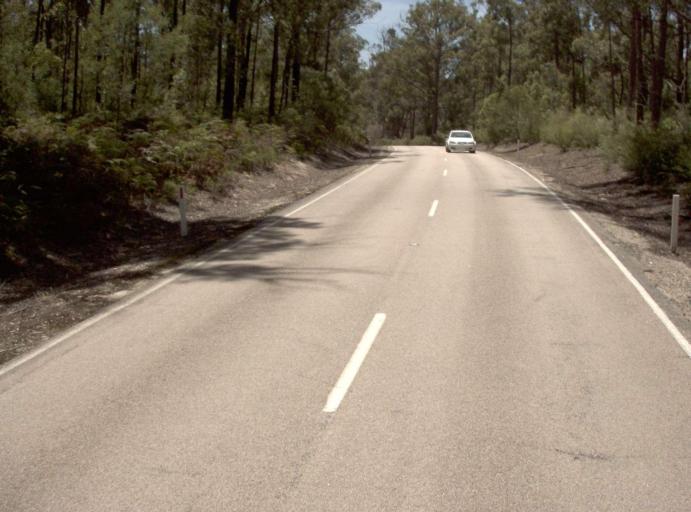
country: AU
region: Victoria
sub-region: East Gippsland
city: Lakes Entrance
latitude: -37.6512
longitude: 147.8899
